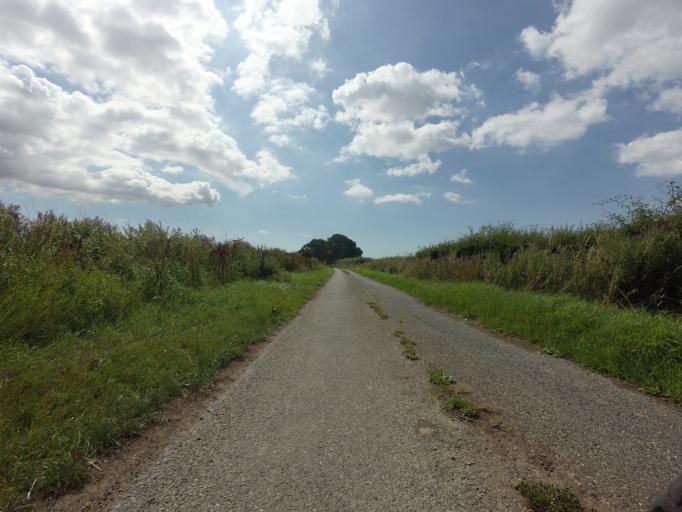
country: GB
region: England
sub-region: Kent
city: Stone
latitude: 51.0508
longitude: 0.7720
